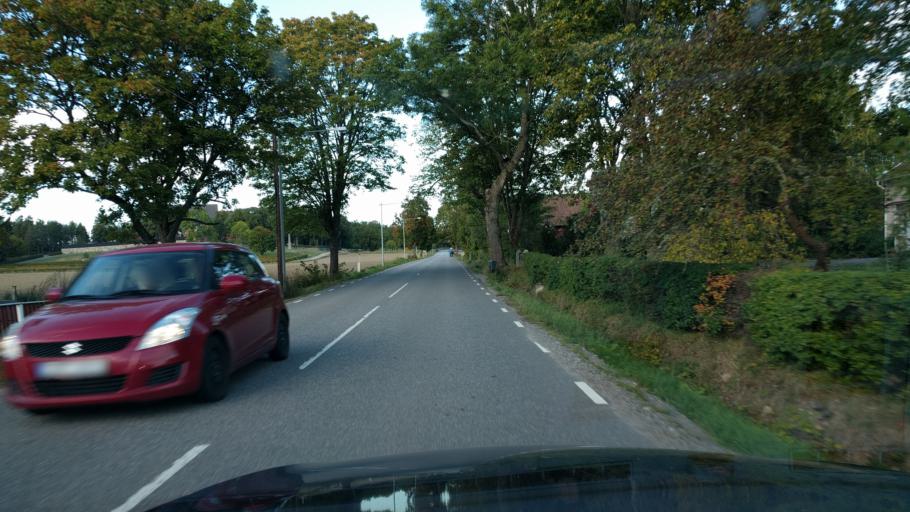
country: SE
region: Uppsala
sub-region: Tierps Kommun
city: Orbyhus
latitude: 60.1599
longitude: 17.6000
